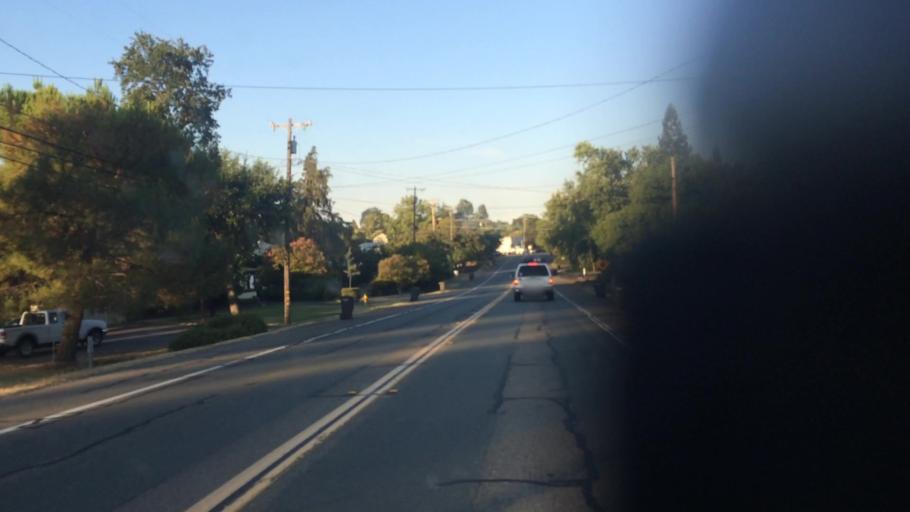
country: US
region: California
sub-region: Amador County
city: Ione
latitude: 38.3563
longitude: -120.9335
